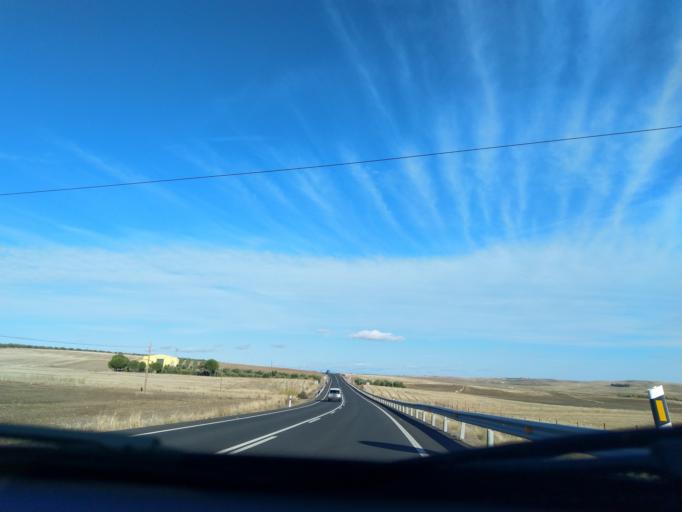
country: ES
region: Extremadura
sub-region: Provincia de Badajoz
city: Ahillones
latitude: 38.2640
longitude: -5.8578
